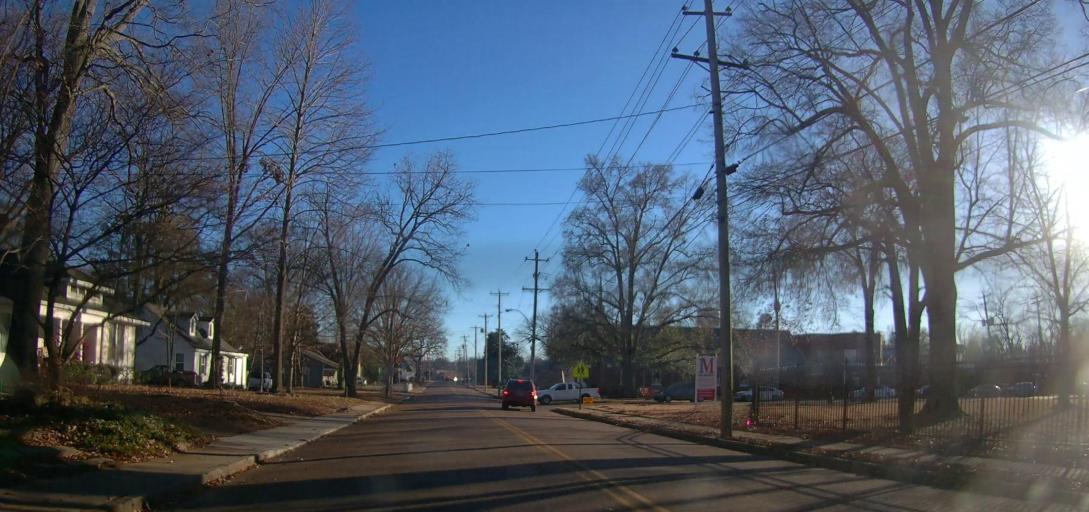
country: US
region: Tennessee
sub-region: Shelby County
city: Millington
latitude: 35.3463
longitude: -89.8947
